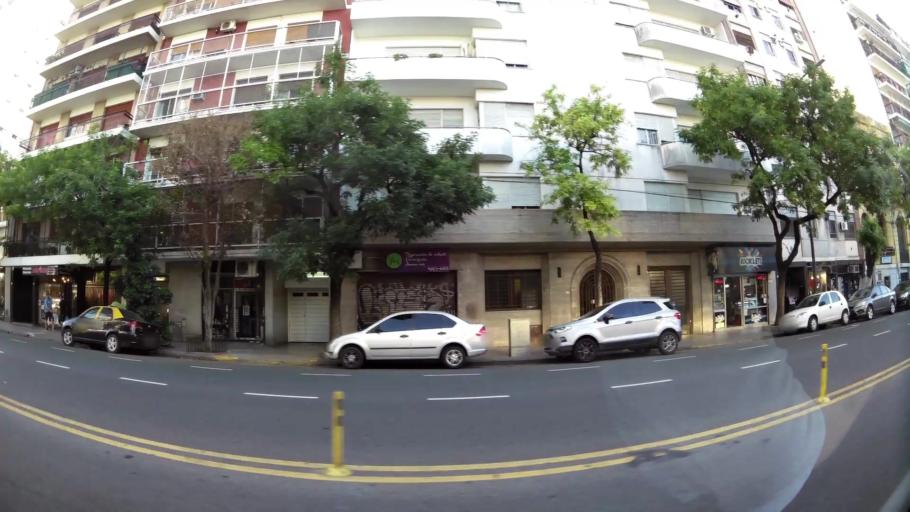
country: AR
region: Buenos Aires F.D.
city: Colegiales
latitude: -34.6165
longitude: -58.4290
